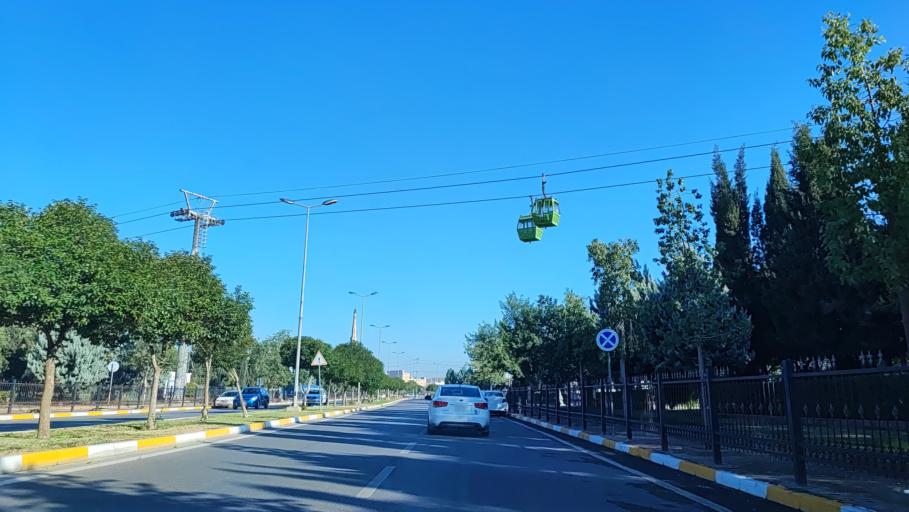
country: IQ
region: Arbil
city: Erbil
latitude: 36.1804
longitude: 44.0035
